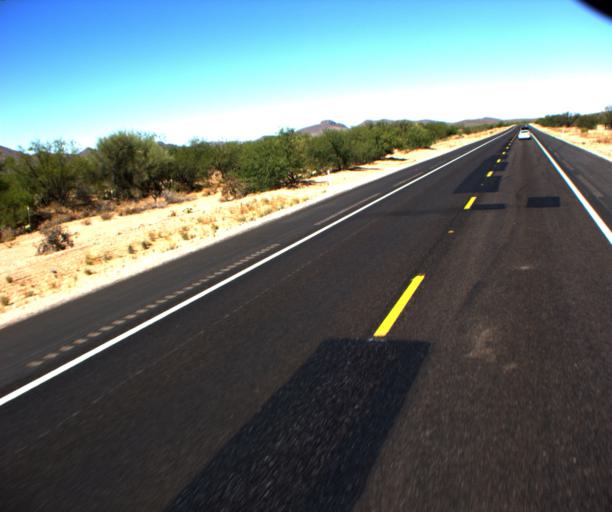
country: US
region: Arizona
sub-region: Pima County
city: Sells
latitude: 31.9221
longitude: -111.8182
